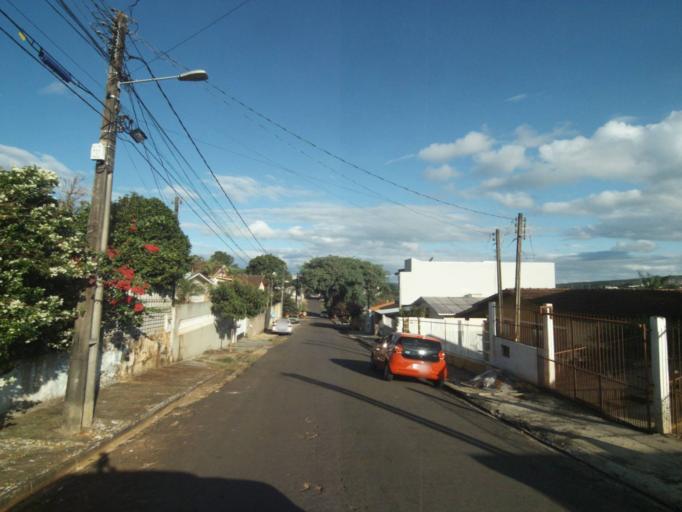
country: BR
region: Parana
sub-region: Telemaco Borba
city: Telemaco Borba
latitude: -24.3316
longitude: -50.6149
